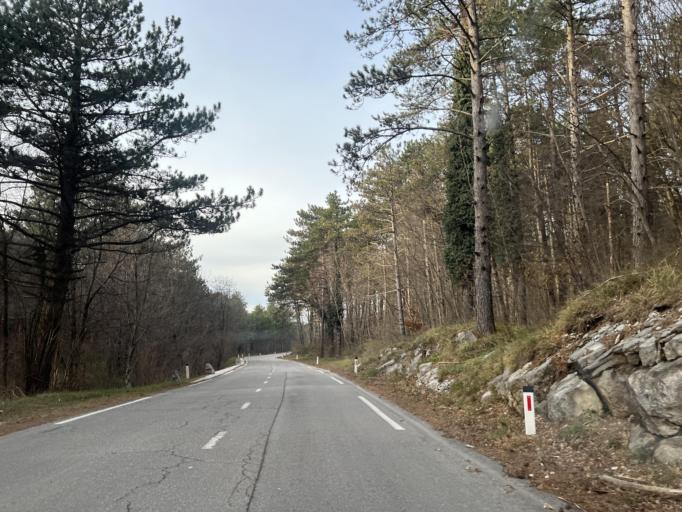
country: SI
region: Nova Gorica
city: Sempas
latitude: 45.9752
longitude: 13.7190
